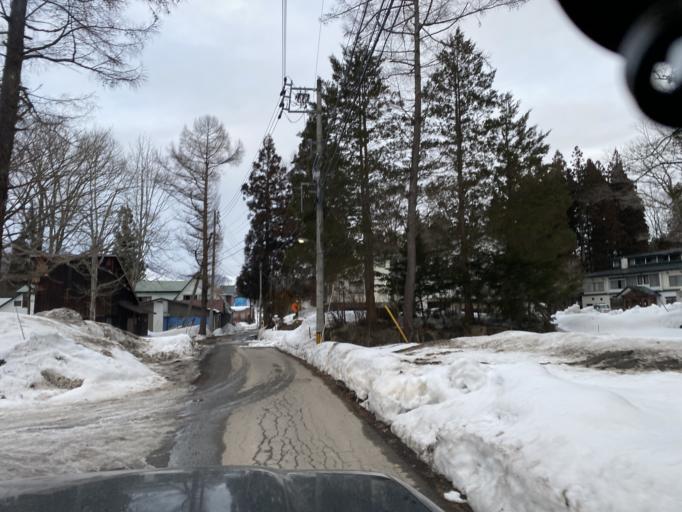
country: JP
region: Nagano
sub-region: Kitaazumi Gun
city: Hakuba
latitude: 36.7151
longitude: 137.8610
